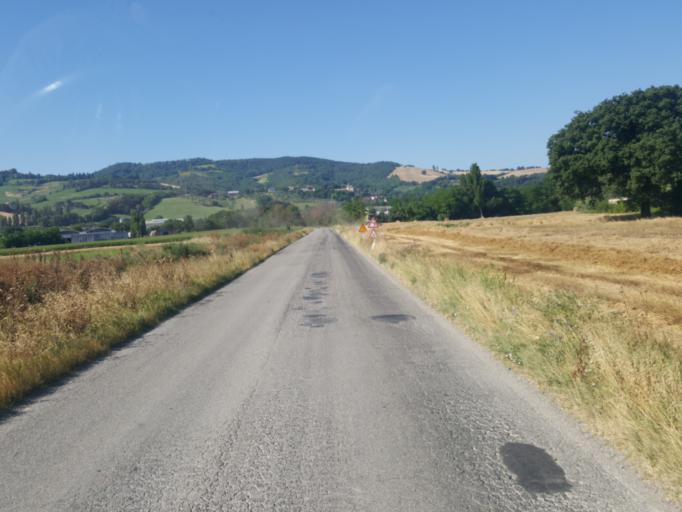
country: IT
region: The Marches
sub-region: Provincia di Pesaro e Urbino
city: Padiglione
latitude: 43.8413
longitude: 12.7190
